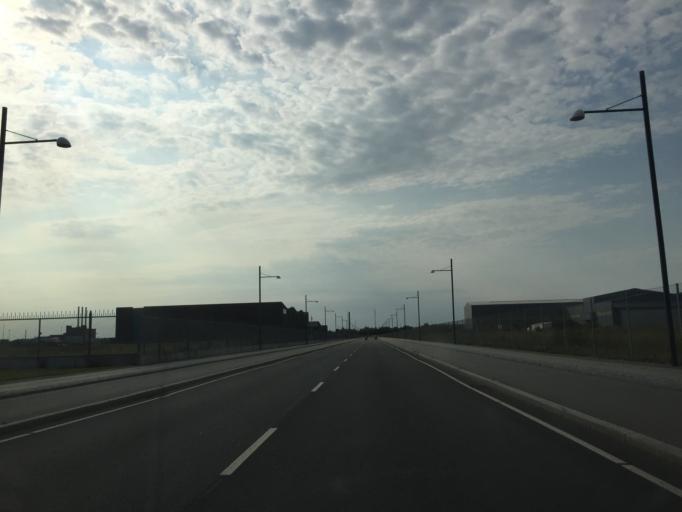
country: DK
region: Capital Region
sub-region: Gentofte Kommune
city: Charlottenlund
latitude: 55.7151
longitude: 12.6145
